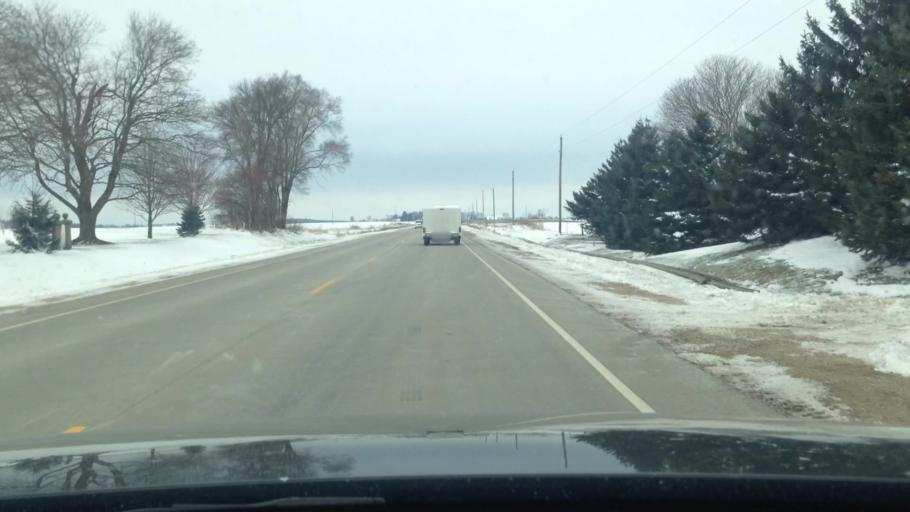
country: US
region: Illinois
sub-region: McHenry County
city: Hebron
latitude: 42.5085
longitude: -88.4426
